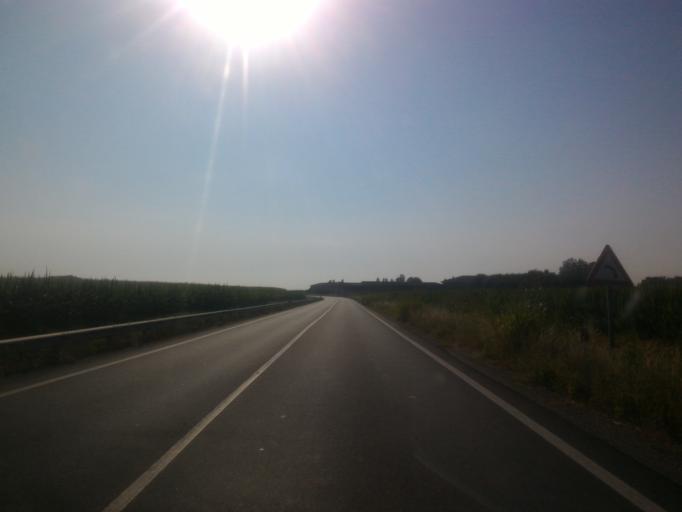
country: IT
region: Piedmont
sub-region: Provincia di Torino
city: Riva
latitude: 44.8785
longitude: 7.3687
